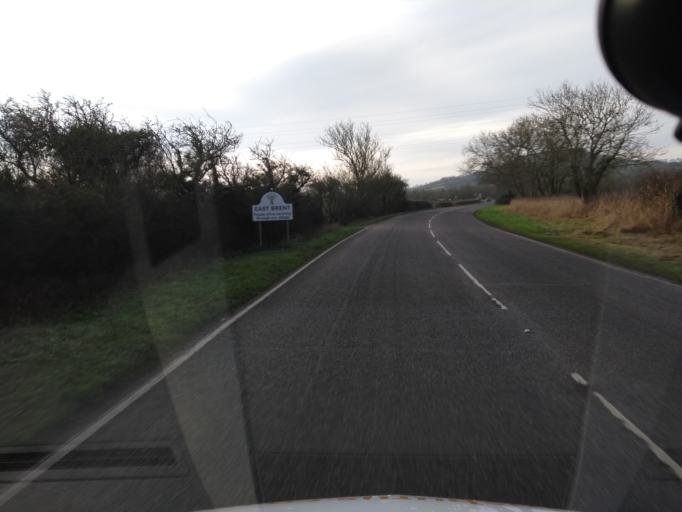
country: GB
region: England
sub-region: North Somerset
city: Bleadon
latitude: 51.2682
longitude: -2.9341
